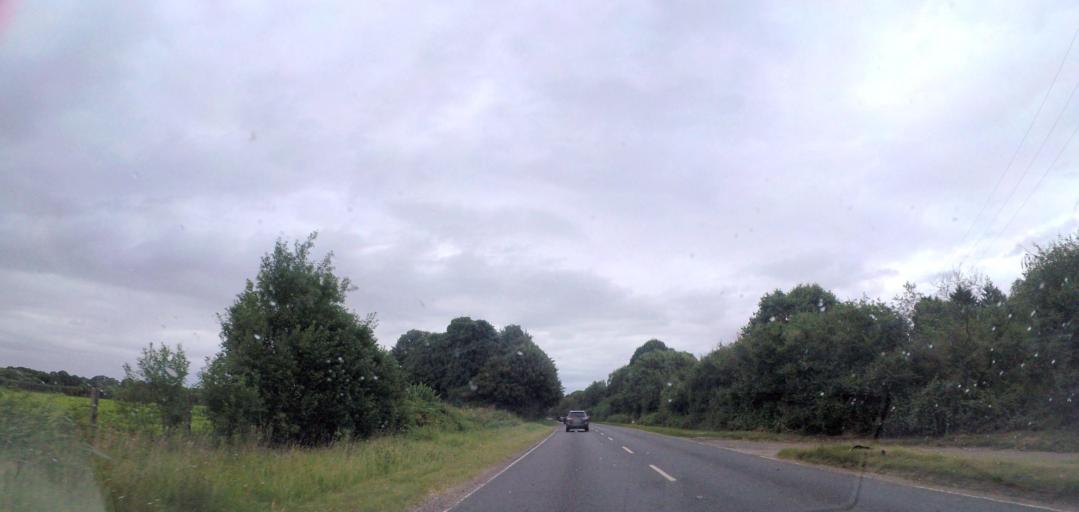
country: GB
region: England
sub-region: Norfolk
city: Spixworth
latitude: 52.6917
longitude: 1.3364
